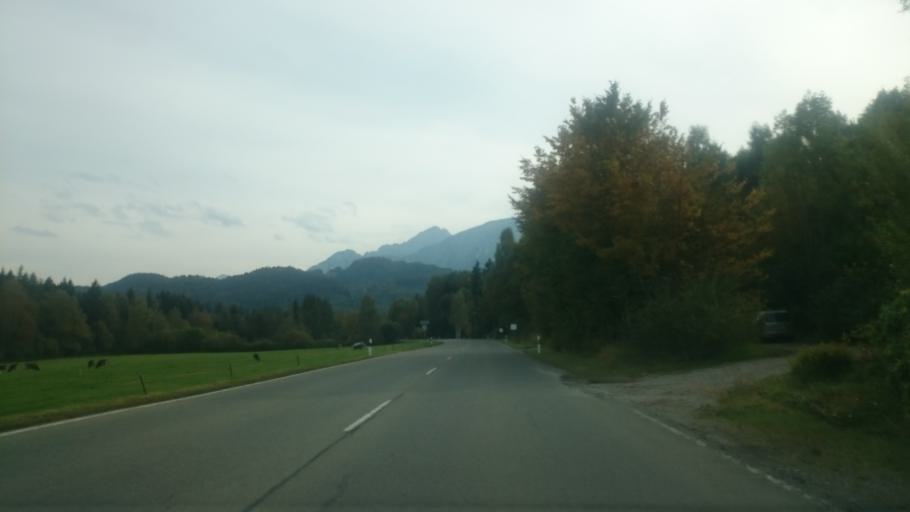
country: AT
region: Tyrol
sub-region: Politischer Bezirk Reutte
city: Vils
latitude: 47.5804
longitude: 10.6531
